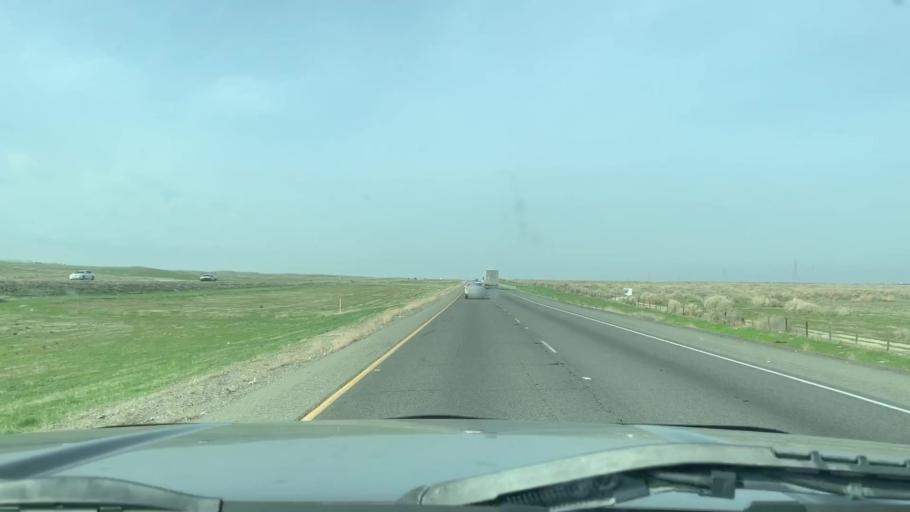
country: US
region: California
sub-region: Fresno County
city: Mendota
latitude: 36.5004
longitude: -120.4535
